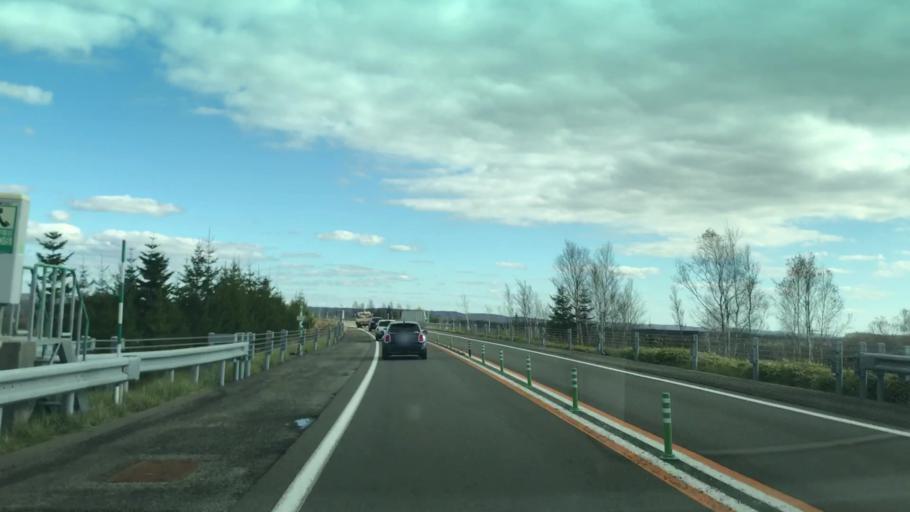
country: JP
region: Hokkaido
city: Chitose
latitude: 42.8814
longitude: 141.6421
